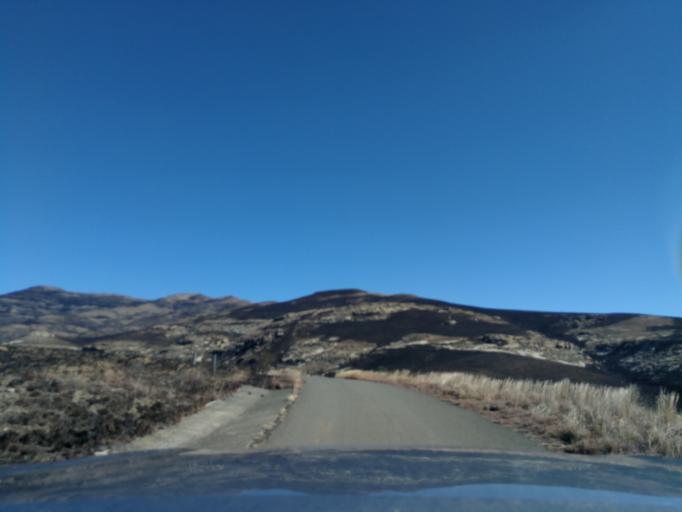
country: ZA
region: Orange Free State
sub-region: Thabo Mofutsanyana District Municipality
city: Phuthaditjhaba
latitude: -28.5132
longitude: 28.6190
